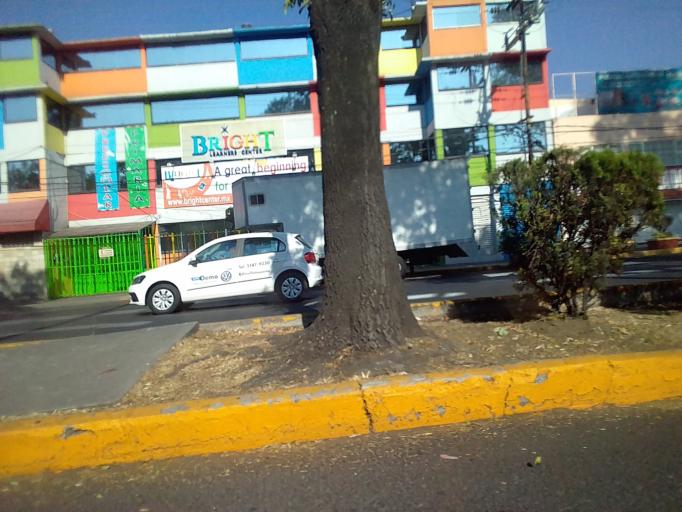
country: MX
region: Mexico
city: Naucalpan de Juarez
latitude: 19.4920
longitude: -99.2275
